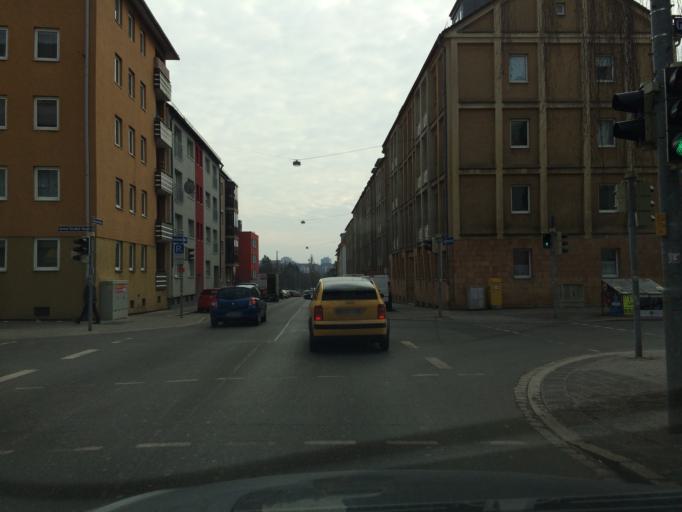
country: DE
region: Bavaria
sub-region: Regierungsbezirk Mittelfranken
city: Nuernberg
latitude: 49.4567
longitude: 11.0979
